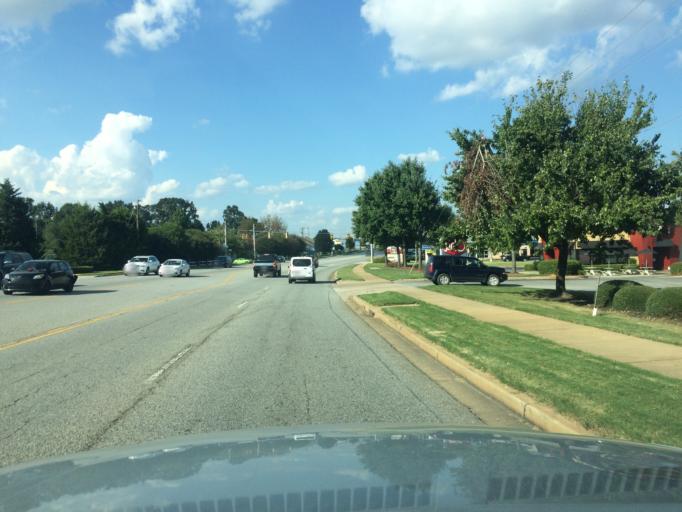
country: US
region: South Carolina
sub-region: Greenville County
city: Simpsonville
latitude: 34.7058
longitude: -82.2578
